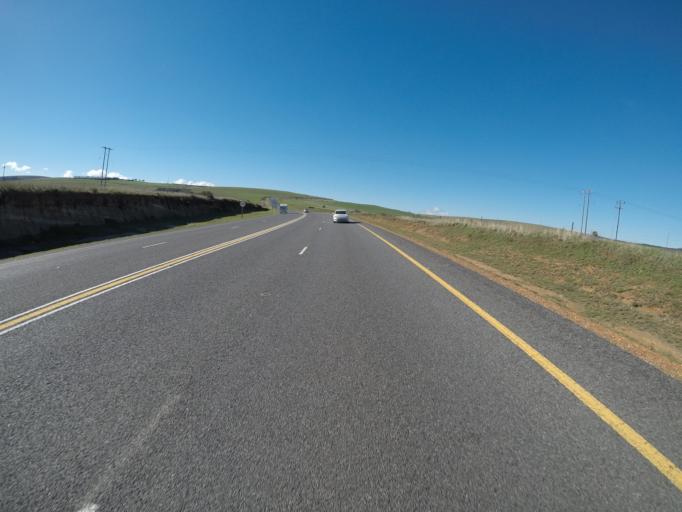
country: ZA
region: Western Cape
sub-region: Overberg District Municipality
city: Caledon
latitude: -34.2348
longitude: 19.2578
